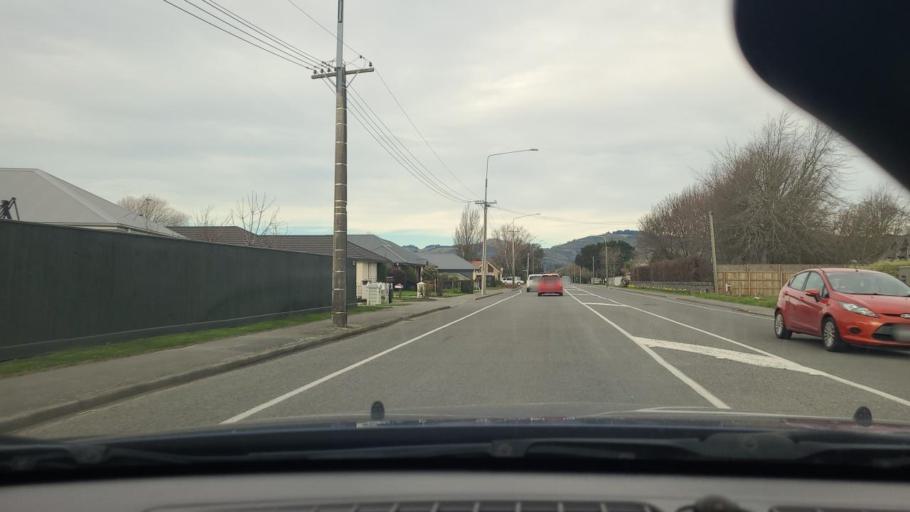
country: NZ
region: Canterbury
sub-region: Selwyn District
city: Prebbleton
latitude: -43.5809
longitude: 172.5592
